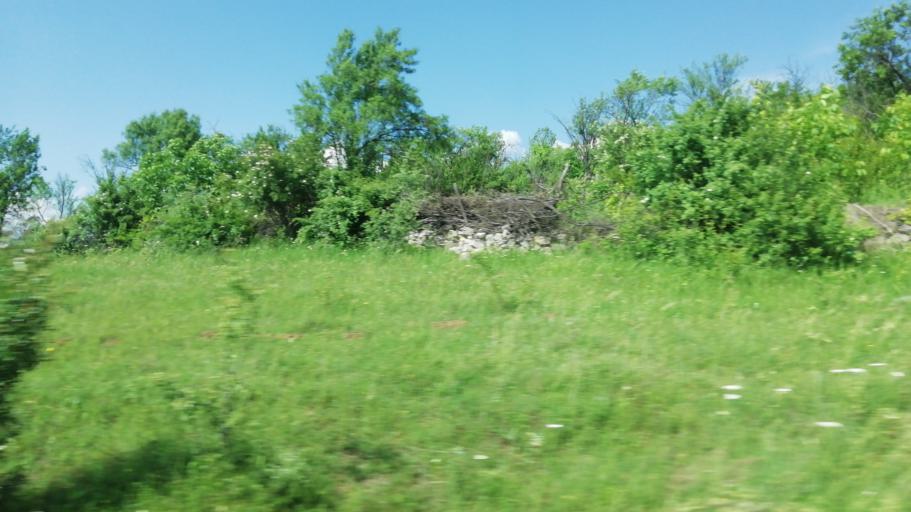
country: TR
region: Karabuk
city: Karabuk
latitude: 41.1252
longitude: 32.5759
